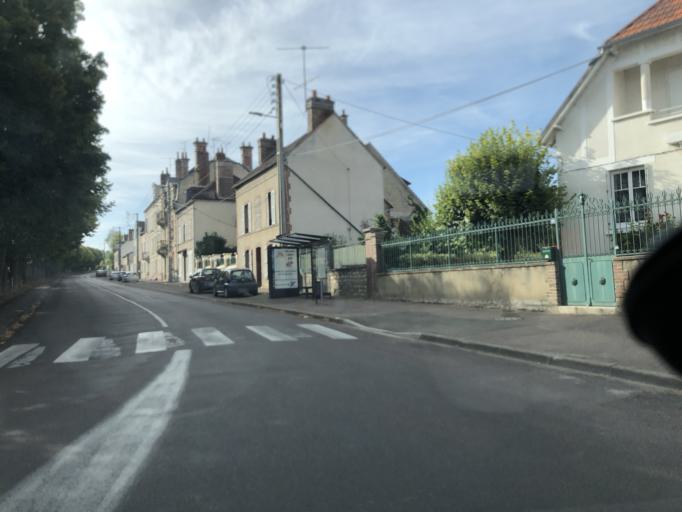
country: FR
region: Bourgogne
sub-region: Departement de l'Yonne
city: Joigny
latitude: 47.9834
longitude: 3.4027
